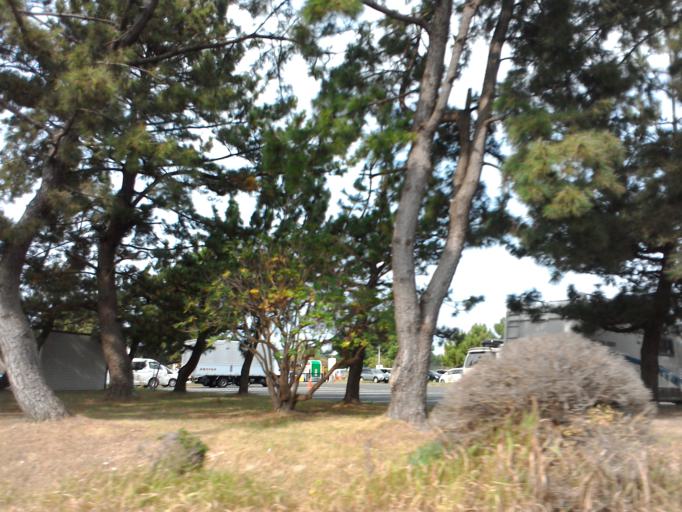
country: JP
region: Shizuoka
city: Kosai-shi
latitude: 34.6962
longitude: 137.6082
